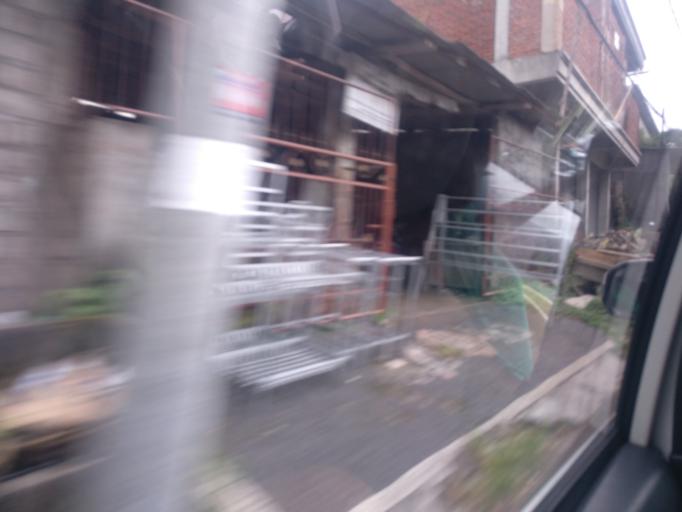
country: ID
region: Bali
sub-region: Kabupaten Gianyar
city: Ubud
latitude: -8.5177
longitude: 115.2678
